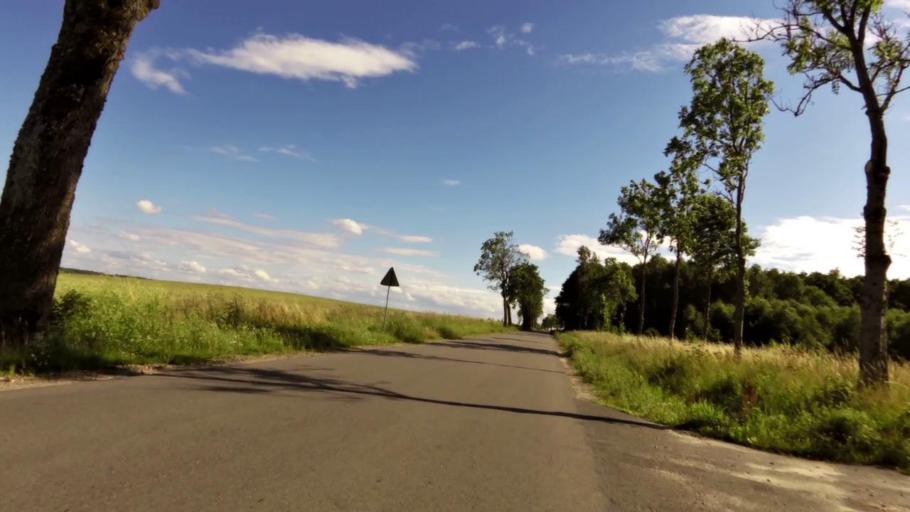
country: PL
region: West Pomeranian Voivodeship
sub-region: Powiat slawienski
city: Slawno
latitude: 54.4519
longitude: 16.7384
